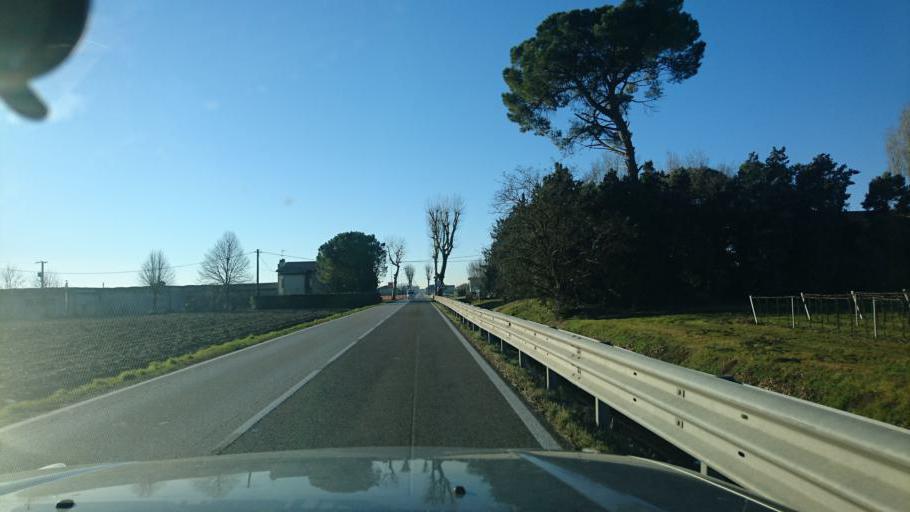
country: IT
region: Veneto
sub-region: Provincia di Venezia
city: Pegolotte
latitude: 45.2041
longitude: 12.0392
